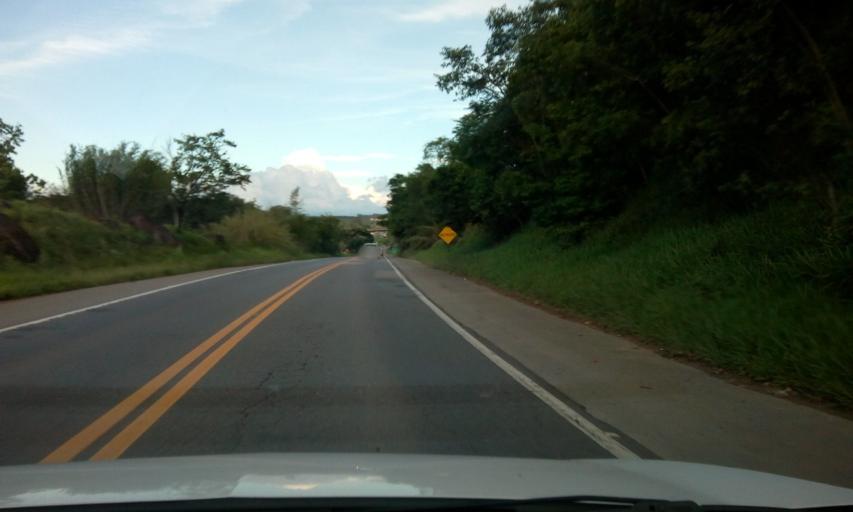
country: BR
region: Sao Paulo
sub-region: Itatiba
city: Itatiba
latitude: -22.9950
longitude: -46.8030
